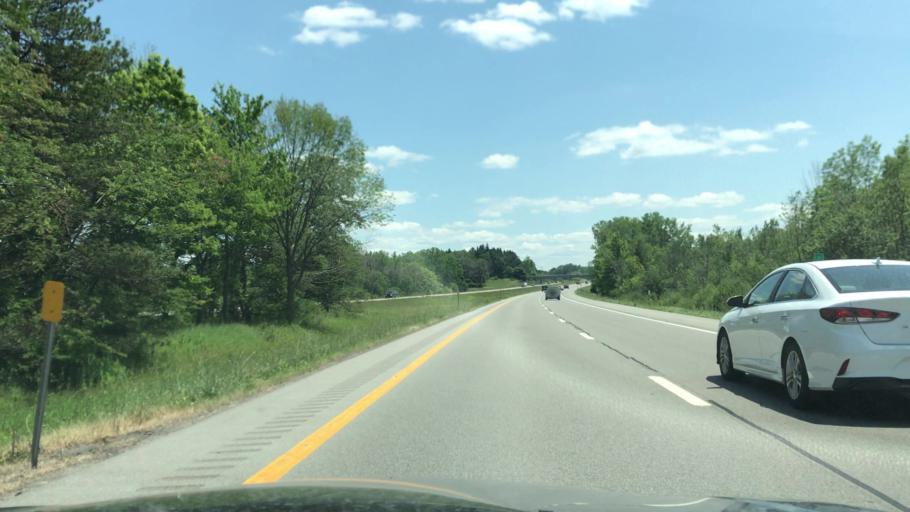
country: US
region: New York
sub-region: Erie County
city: Elma Center
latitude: 42.8246
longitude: -78.6701
